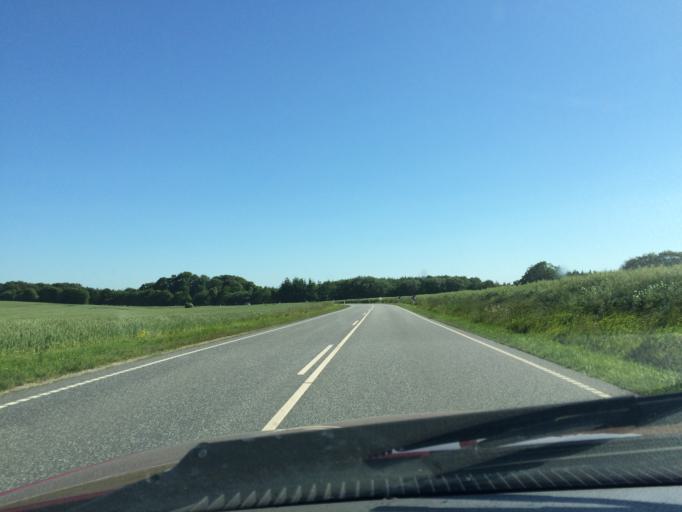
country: DK
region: Central Jutland
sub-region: Viborg Kommune
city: Bjerringbro
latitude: 56.3235
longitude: 9.6779
